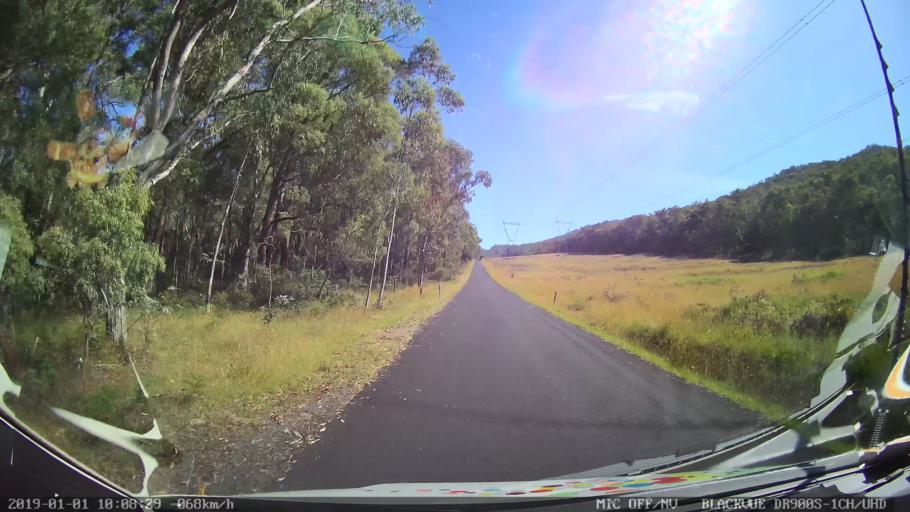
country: AU
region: New South Wales
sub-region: Snowy River
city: Jindabyne
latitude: -36.1591
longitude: 148.1576
